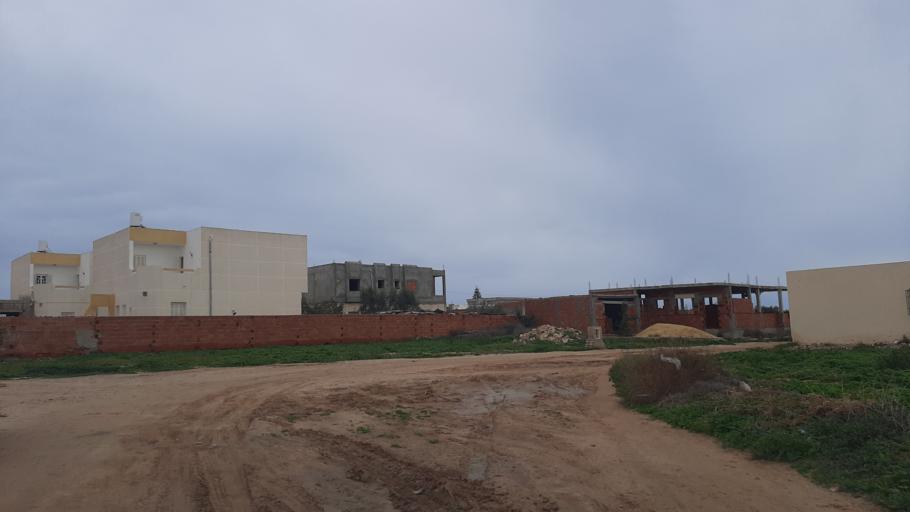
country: TN
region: Safaqis
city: Al Qarmadah
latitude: 34.7987
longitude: 10.8545
